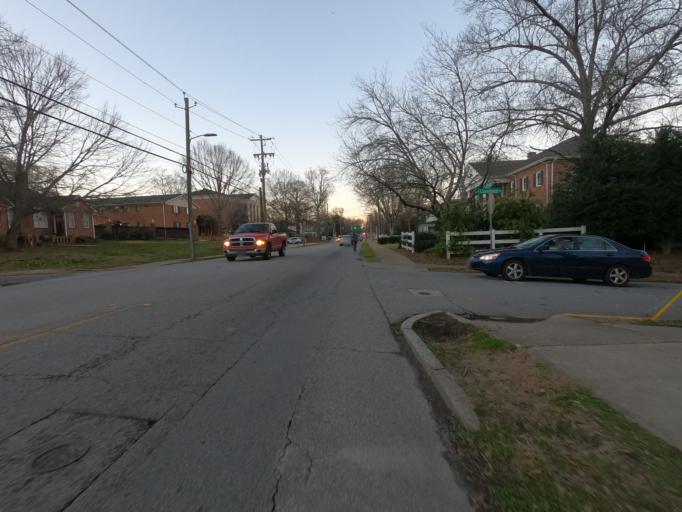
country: US
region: Georgia
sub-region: Clarke County
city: Athens
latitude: 33.9447
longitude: -83.3878
